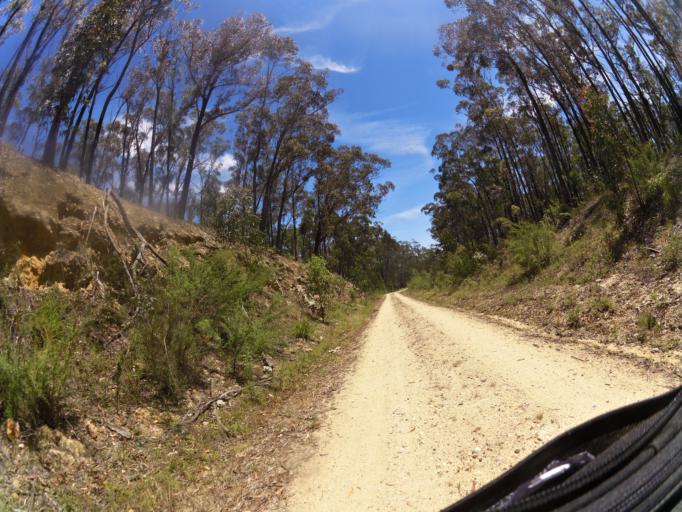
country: AU
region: Victoria
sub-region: East Gippsland
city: Lakes Entrance
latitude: -37.7598
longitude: 147.9348
